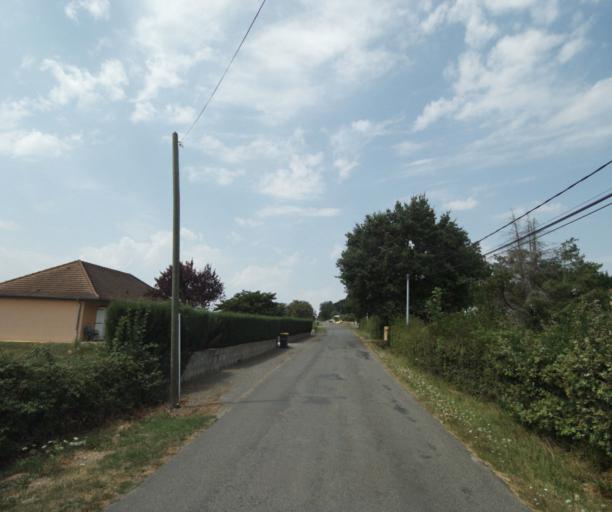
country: FR
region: Bourgogne
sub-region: Departement de Saone-et-Loire
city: Gueugnon
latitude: 46.5977
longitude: 4.0195
